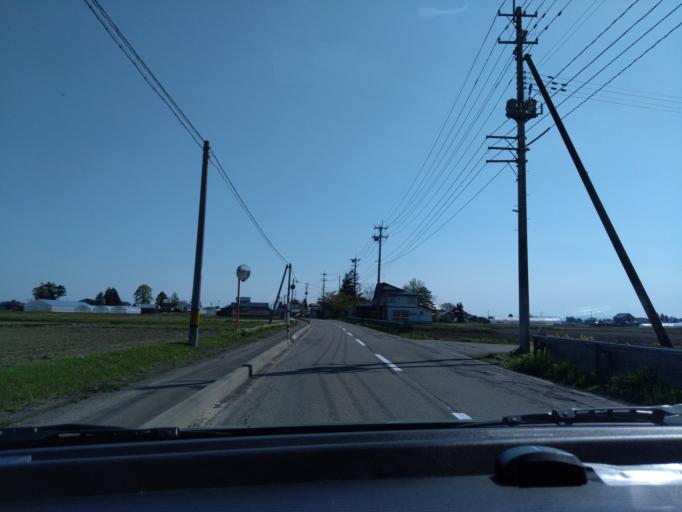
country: JP
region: Akita
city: Omagari
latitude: 39.4470
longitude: 140.5676
